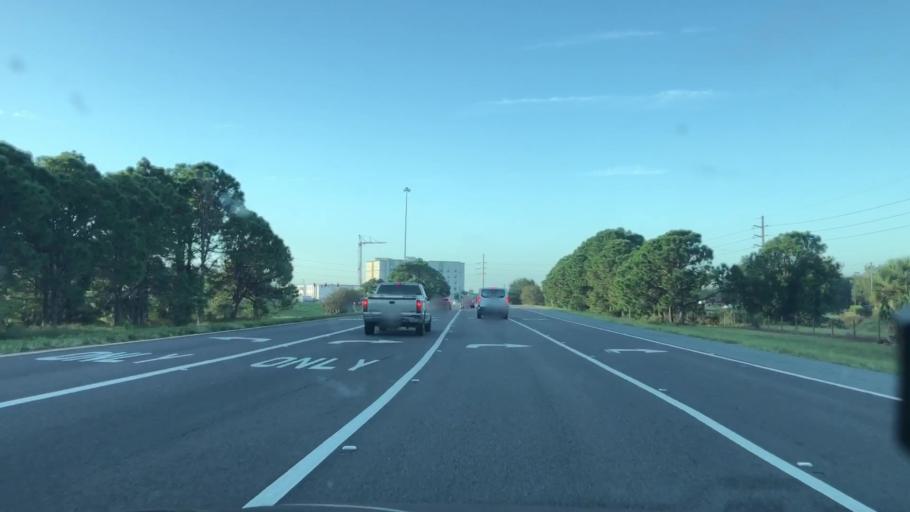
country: US
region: Florida
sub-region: Sarasota County
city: Fruitville
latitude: 27.3408
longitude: -82.4482
